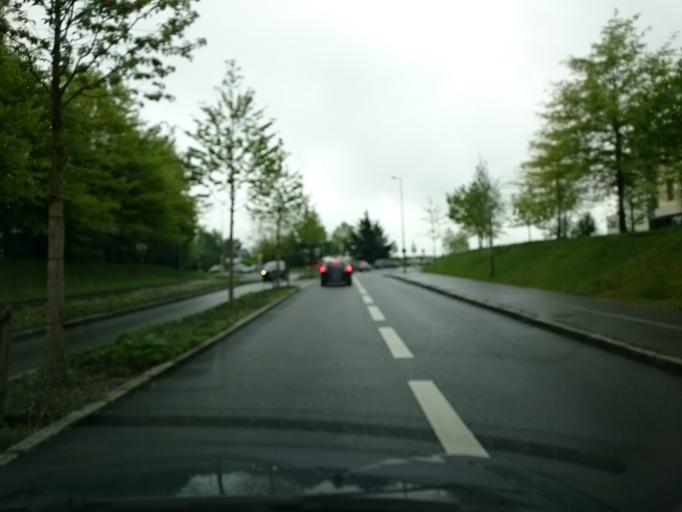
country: FR
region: Brittany
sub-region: Departement d'Ille-et-Vilaine
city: Saint-Gregoire
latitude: 48.1445
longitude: -1.6865
